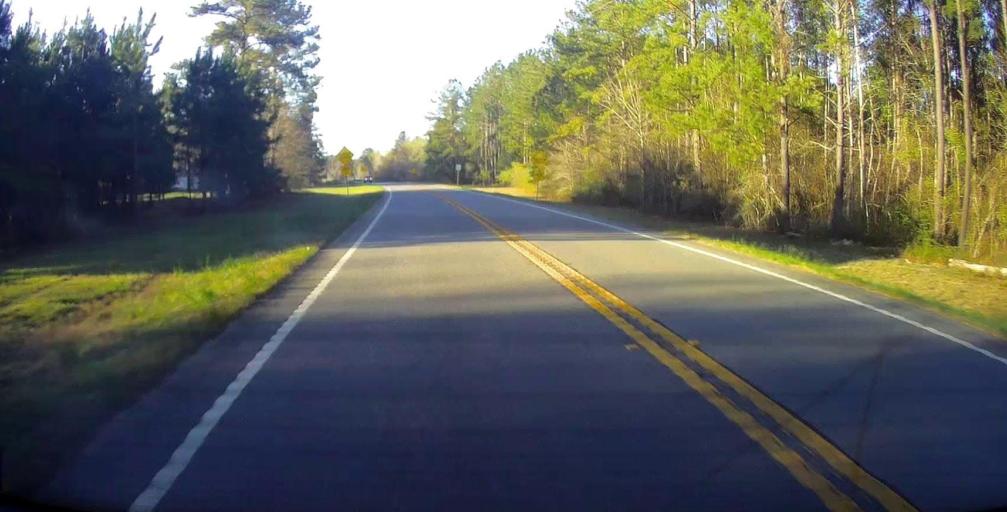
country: US
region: Georgia
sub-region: Wilcox County
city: Abbeville
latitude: 32.0116
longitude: -83.2482
